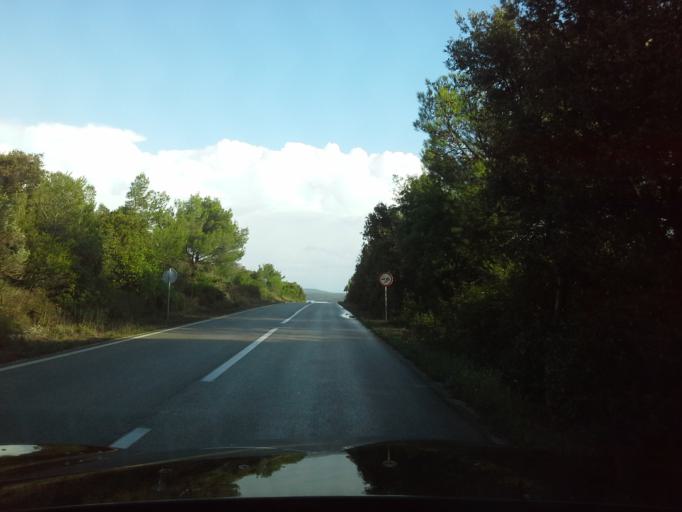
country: HR
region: Primorsko-Goranska
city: Mali Losinj
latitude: 44.5821
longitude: 14.4123
